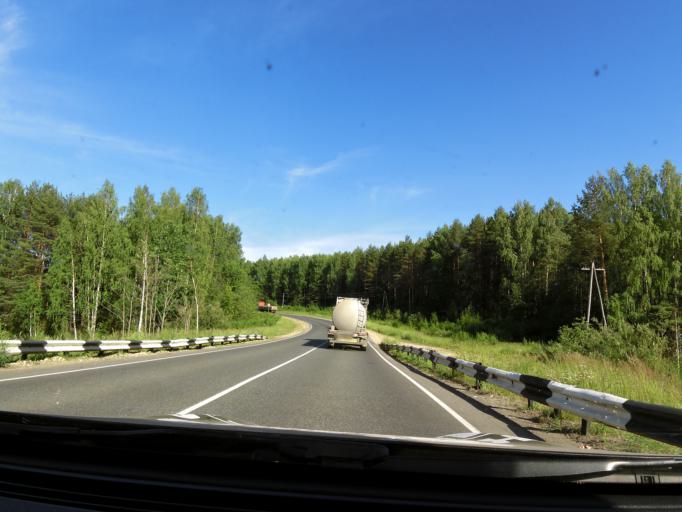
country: RU
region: Kirov
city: Belaya Kholunitsa
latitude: 58.9042
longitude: 50.9484
